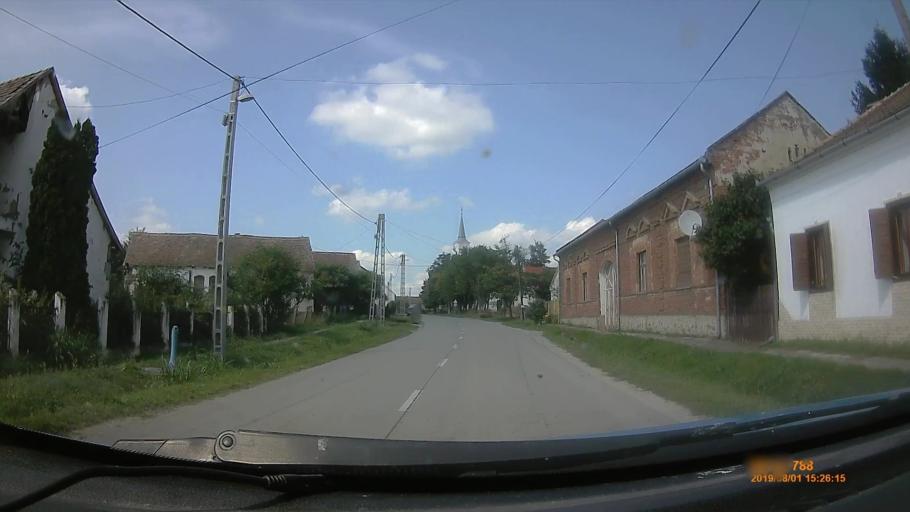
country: HU
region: Baranya
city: Sellye
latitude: 45.9007
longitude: 17.8572
